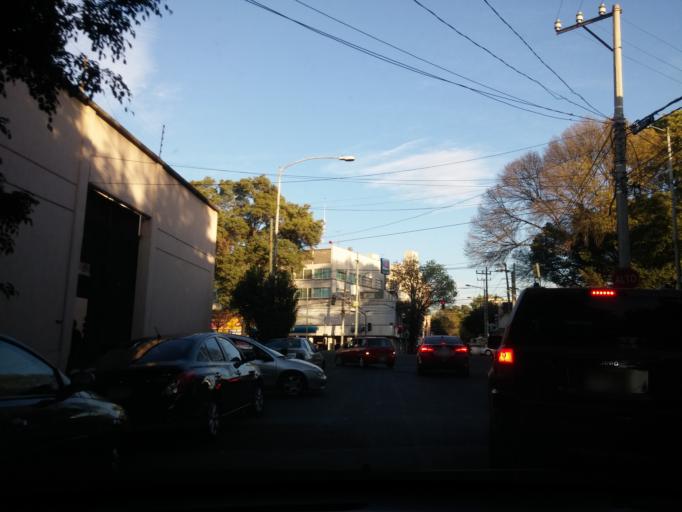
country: MX
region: Mexico City
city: Azcapotzalco
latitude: 19.4669
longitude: -99.1777
